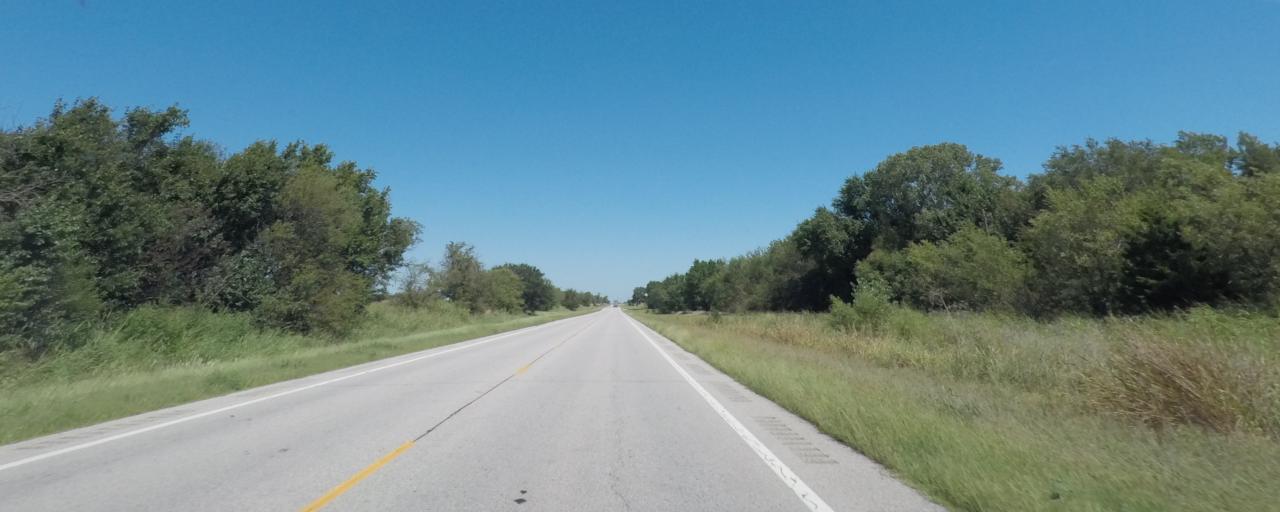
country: US
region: Kansas
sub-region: Sumner County
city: Belle Plaine
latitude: 37.3797
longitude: -97.3850
